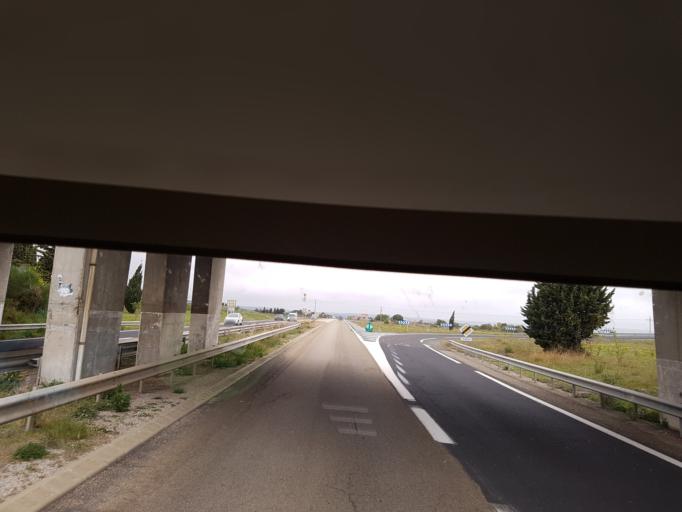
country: FR
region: Languedoc-Roussillon
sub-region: Departement de l'Aude
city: Leucate
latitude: 42.9363
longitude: 2.9914
